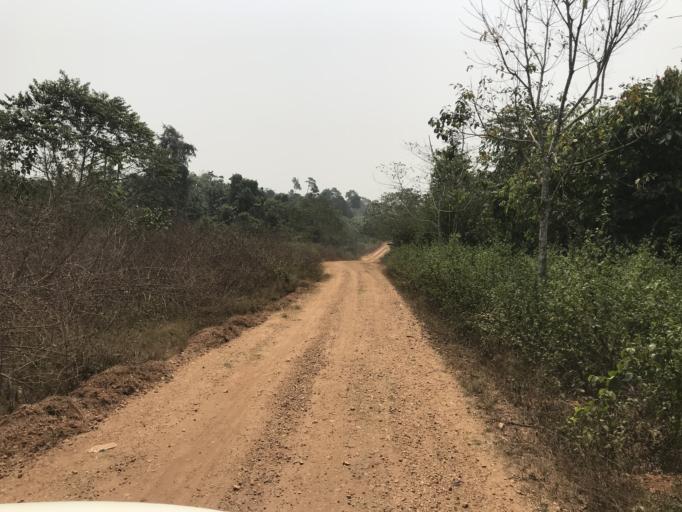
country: NG
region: Osun
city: Ifetedo
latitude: 7.0317
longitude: 4.4759
